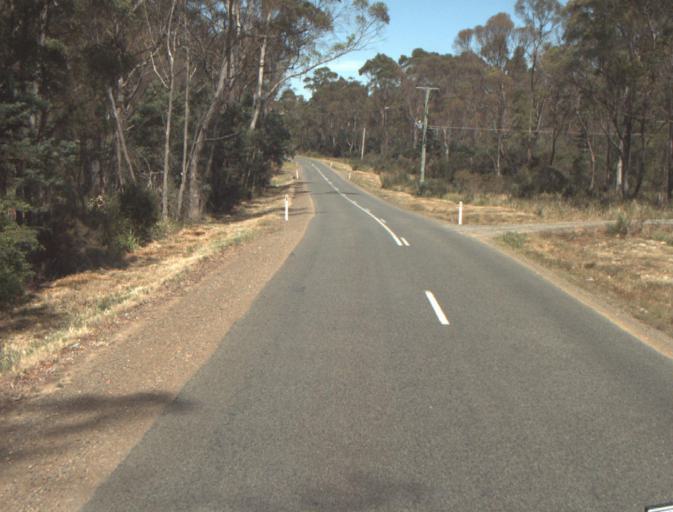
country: AU
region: Tasmania
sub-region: Launceston
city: Mayfield
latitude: -41.3315
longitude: 147.1406
